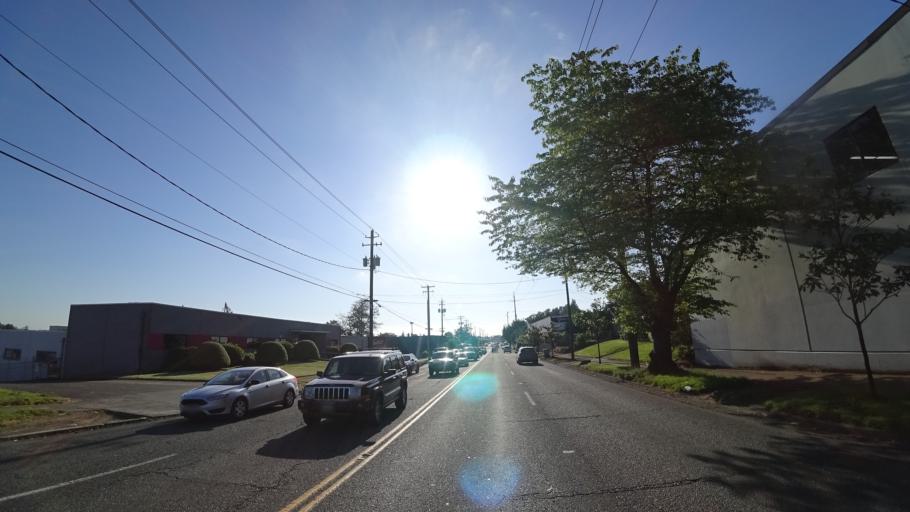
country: US
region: Oregon
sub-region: Multnomah County
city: Portland
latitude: 45.5773
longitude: -122.6585
